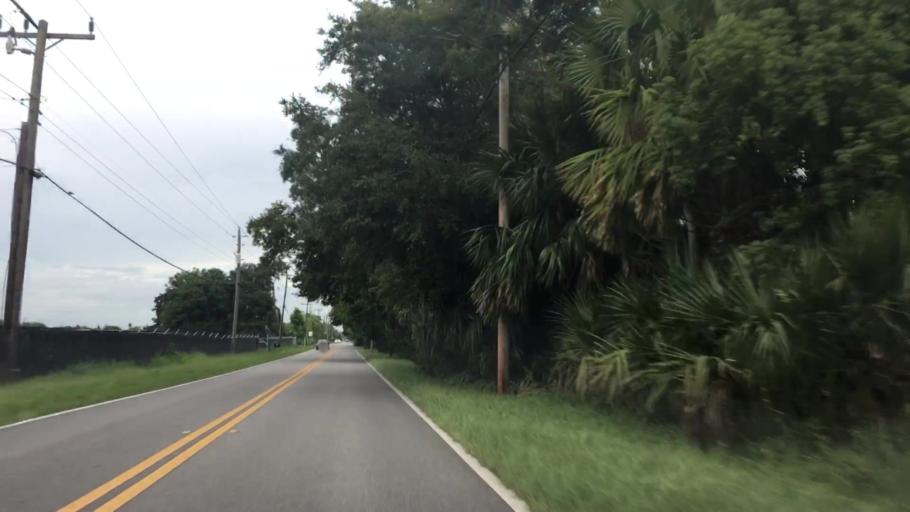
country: US
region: Florida
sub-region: Seminole County
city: Midway
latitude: 28.8014
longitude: -81.2206
